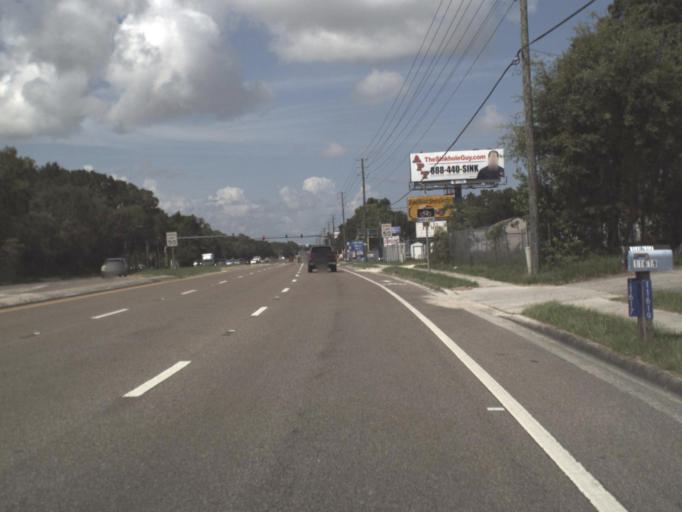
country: US
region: Florida
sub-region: Pasco County
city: Bayonet Point
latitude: 28.3381
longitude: -82.6229
